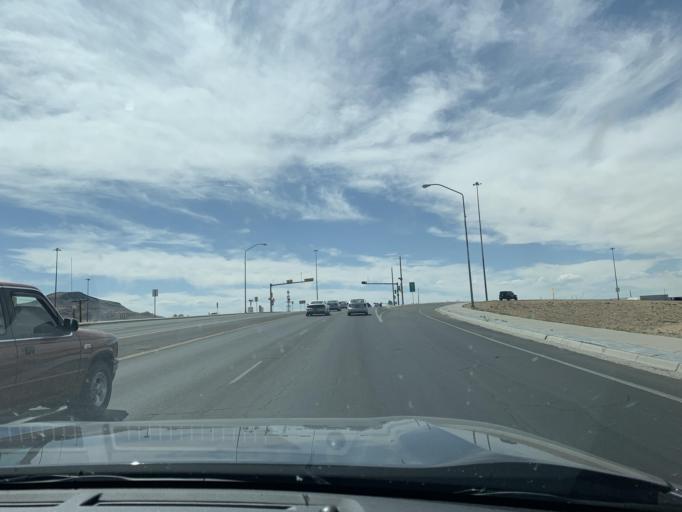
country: US
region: New Mexico
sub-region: Valencia County
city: Los Lunas
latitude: 34.8139
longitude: -106.7589
